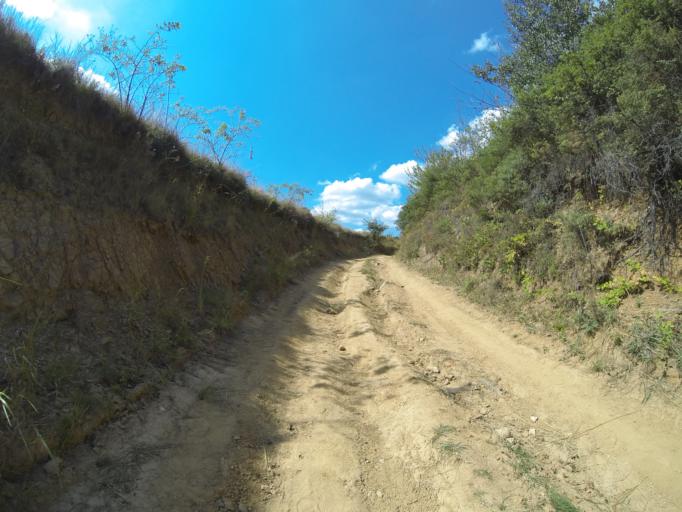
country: RO
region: Mehedinti
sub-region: Comuna Svinita
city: Svinita
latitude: 44.5534
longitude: 22.1350
